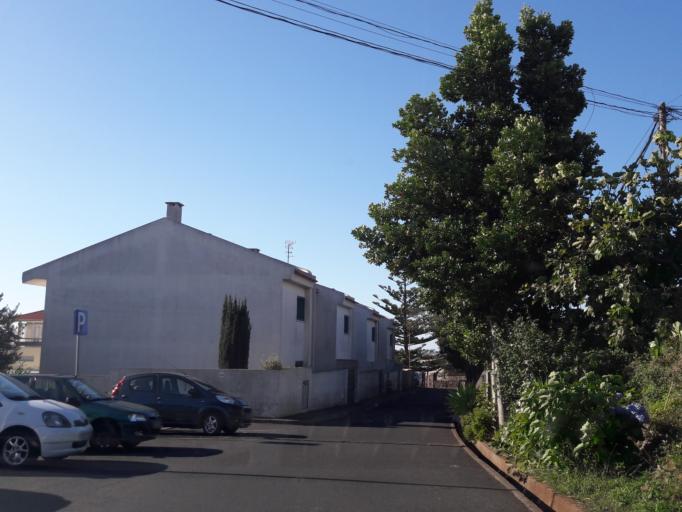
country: PT
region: Madeira
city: Canico
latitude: 32.6531
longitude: -16.8576
